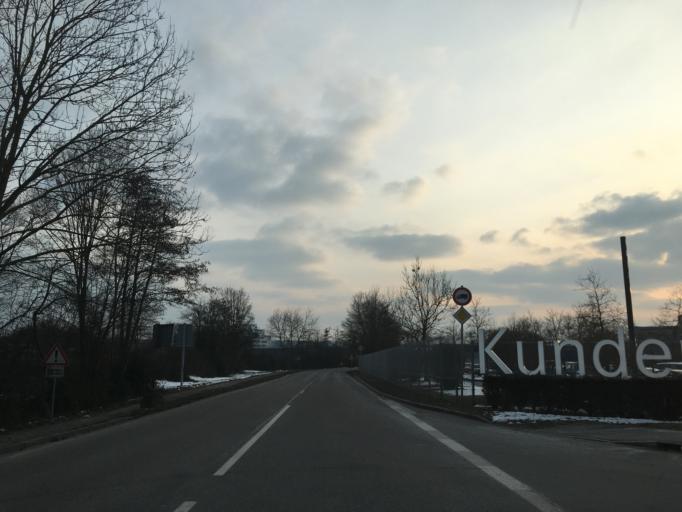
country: DE
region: Baden-Wuerttemberg
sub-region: Regierungsbezirk Stuttgart
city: Sindelfingen
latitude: 48.6952
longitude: 9.0005
